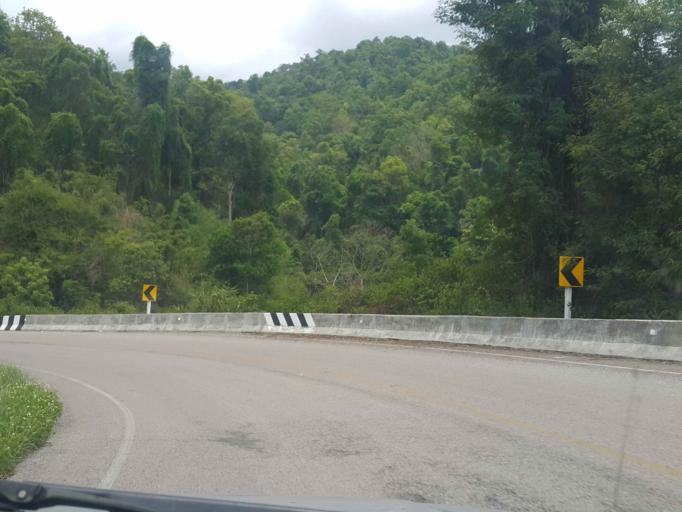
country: TH
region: Phayao
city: Chiang Muan
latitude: 18.9251
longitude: 100.1031
